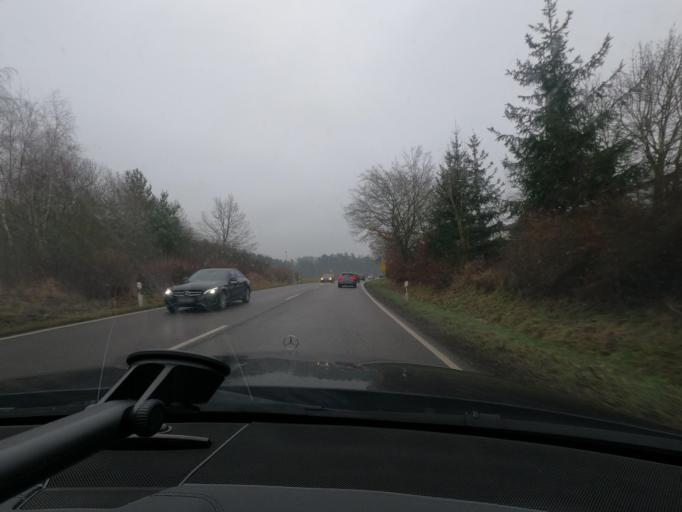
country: DE
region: Hesse
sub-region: Regierungsbezirk Kassel
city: Wolfhagen
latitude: 51.3233
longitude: 9.1838
